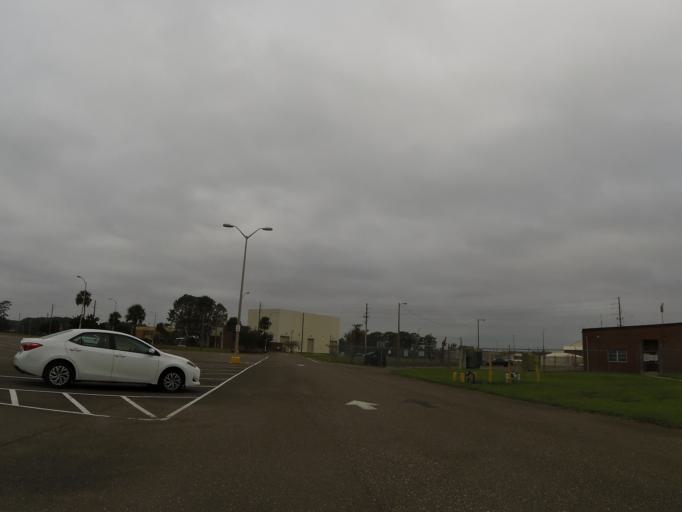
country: US
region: Florida
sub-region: Duval County
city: Baldwin
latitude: 30.2220
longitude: -81.8811
